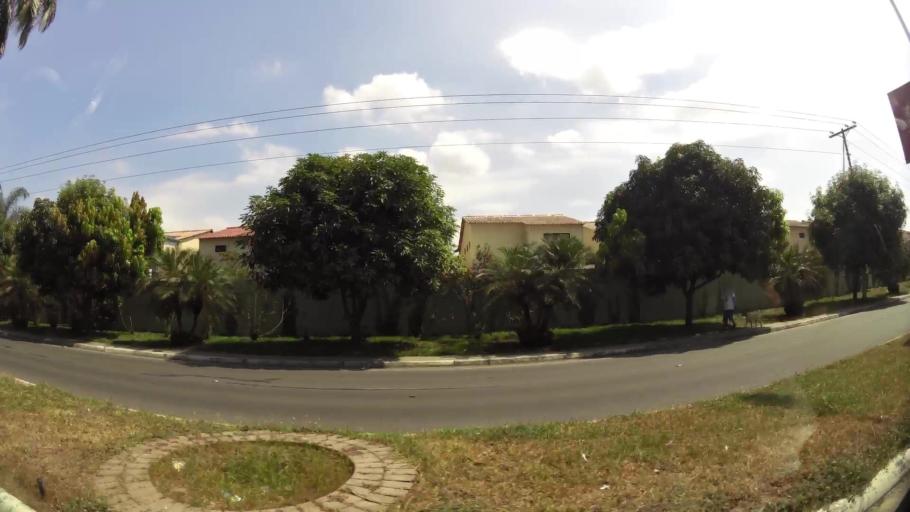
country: EC
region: Guayas
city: El Triunfo
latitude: -2.0434
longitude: -79.8917
